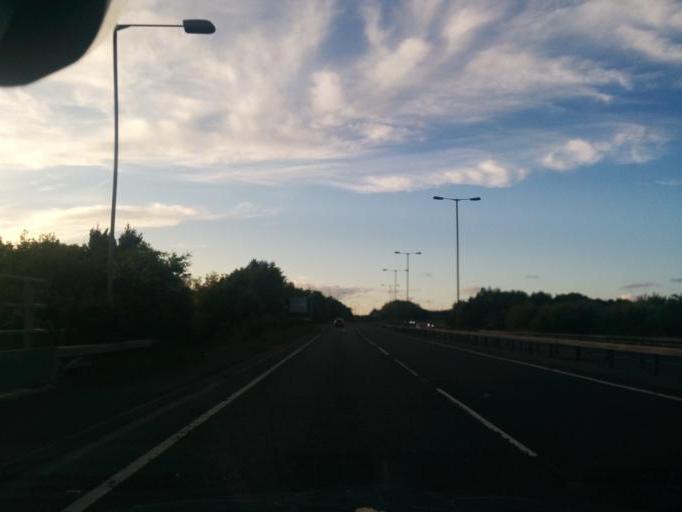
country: GB
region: England
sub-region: Northumberland
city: Bedlington
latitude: 55.1348
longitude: -1.5593
